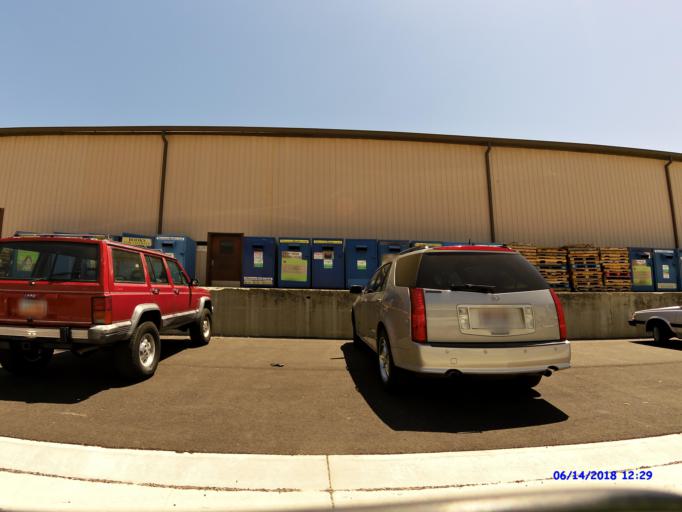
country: US
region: Utah
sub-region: Weber County
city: Harrisville
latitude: 41.2598
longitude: -111.9994
